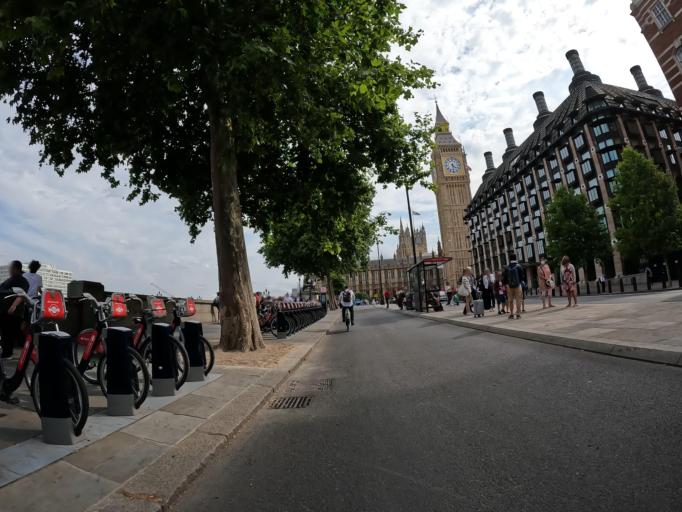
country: GB
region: England
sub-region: Greater London
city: Orpington
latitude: 51.3584
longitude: 0.0561
